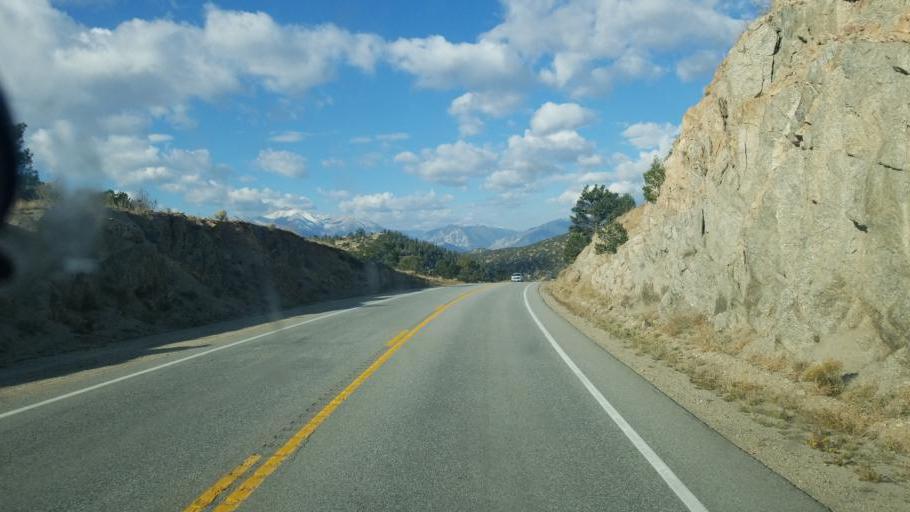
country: US
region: Colorado
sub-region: Chaffee County
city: Buena Vista
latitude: 38.8411
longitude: -105.9995
